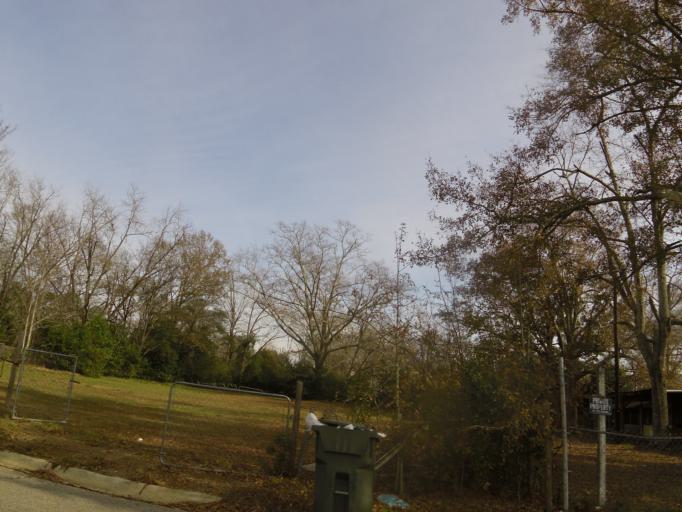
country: US
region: Alabama
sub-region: Houston County
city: Dothan
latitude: 31.2375
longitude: -85.3957
